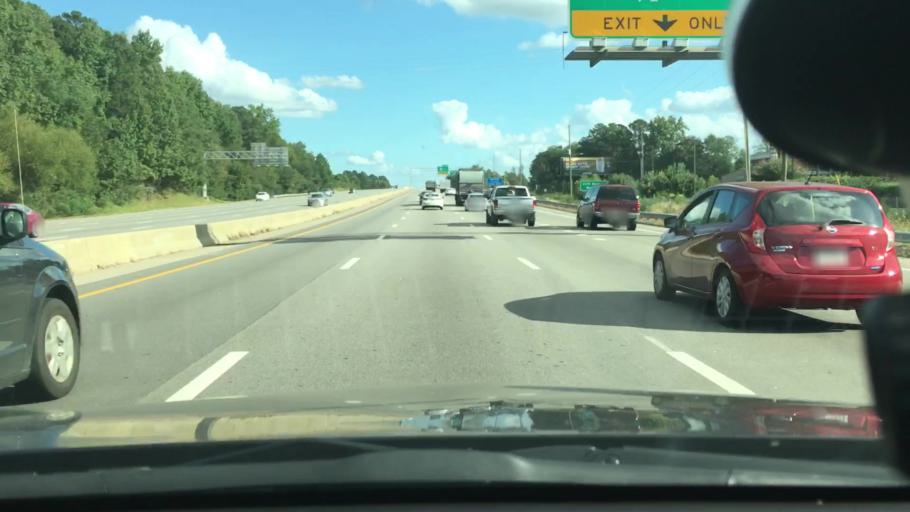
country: US
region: North Carolina
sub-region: Wake County
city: Raleigh
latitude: 35.7992
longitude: -78.5896
